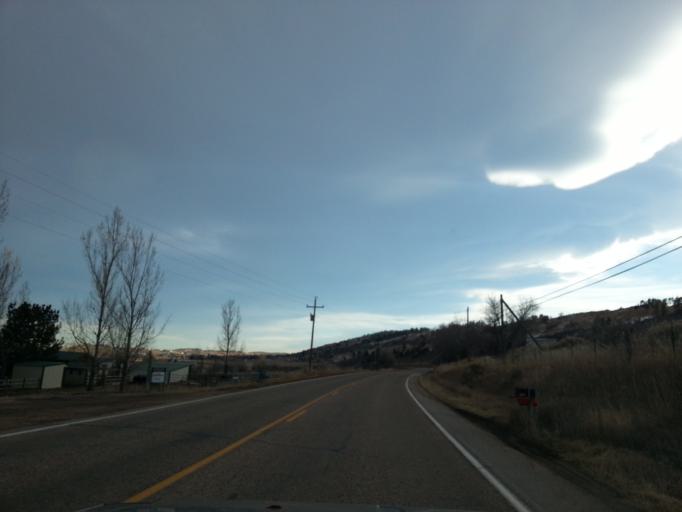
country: US
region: Colorado
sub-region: Larimer County
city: Loveland
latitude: 40.4543
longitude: -105.2048
